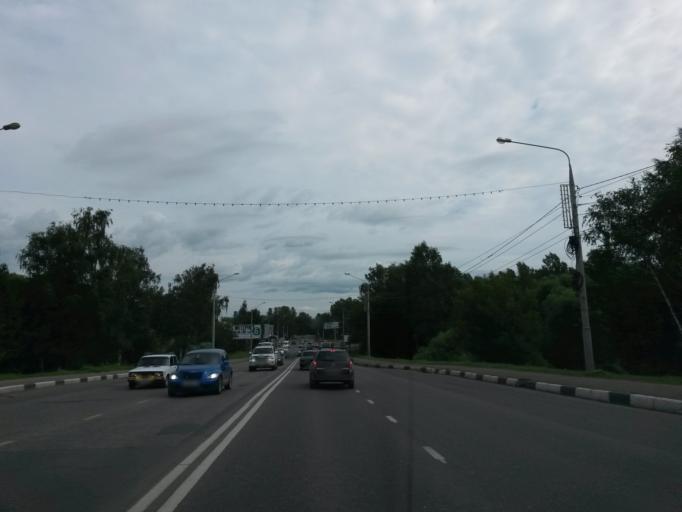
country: RU
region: Jaroslavl
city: Yaroslavl
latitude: 57.6435
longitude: 39.9036
